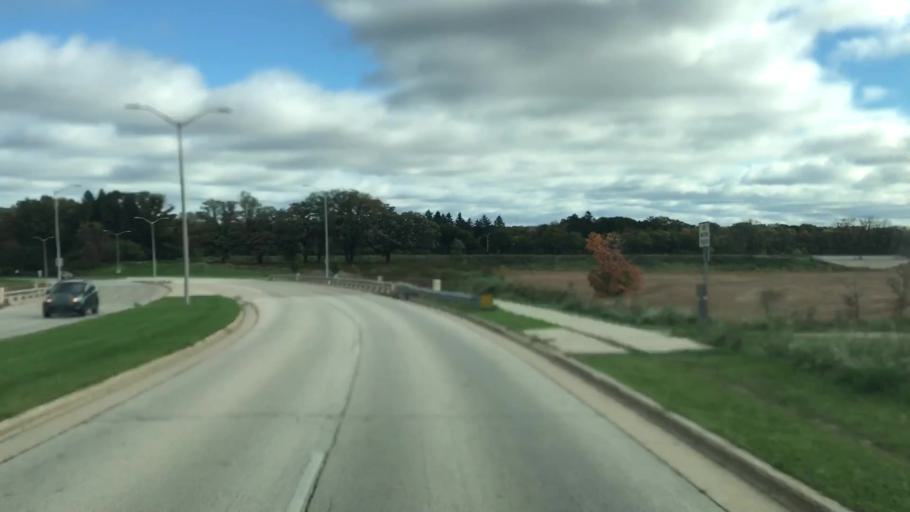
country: US
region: Wisconsin
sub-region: Milwaukee County
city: Wauwatosa
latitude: 43.0528
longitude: -88.0300
